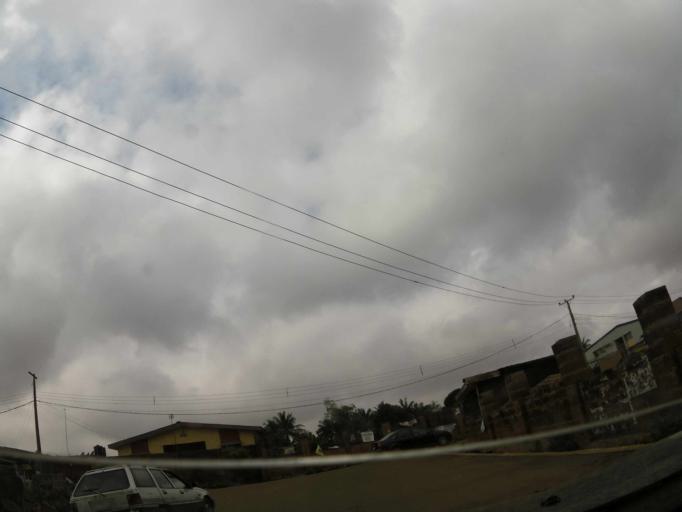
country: NG
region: Oyo
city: Ibadan
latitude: 7.4369
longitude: 3.9507
